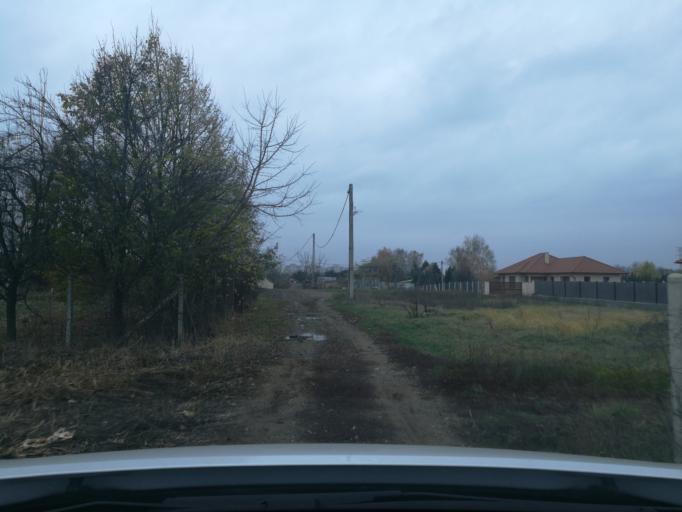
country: HU
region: Szabolcs-Szatmar-Bereg
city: Nyiregyhaza
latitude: 47.9581
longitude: 21.7574
